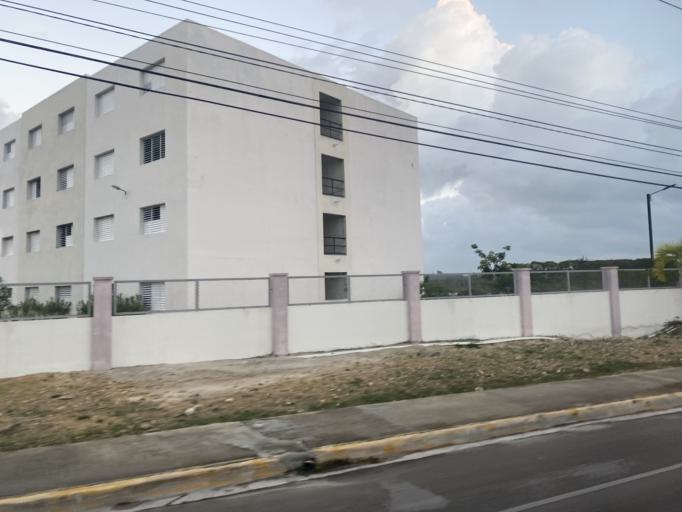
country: DO
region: San Juan
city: Punta Cana
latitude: 18.7066
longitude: -68.4653
